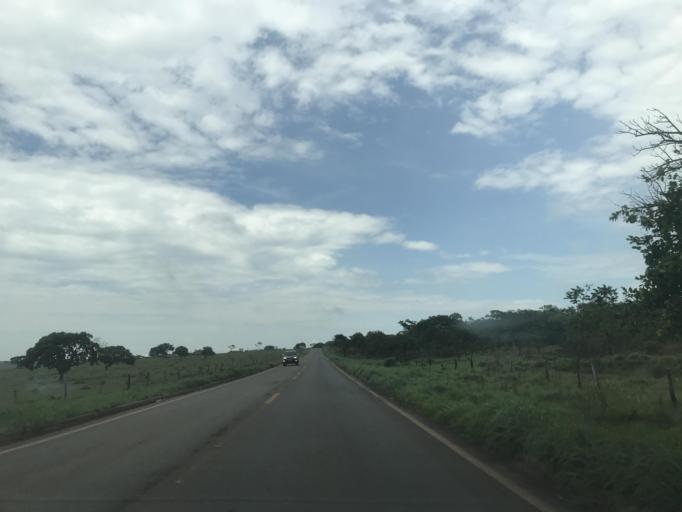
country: BR
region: Goias
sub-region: Luziania
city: Luziania
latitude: -16.2710
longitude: -47.9869
